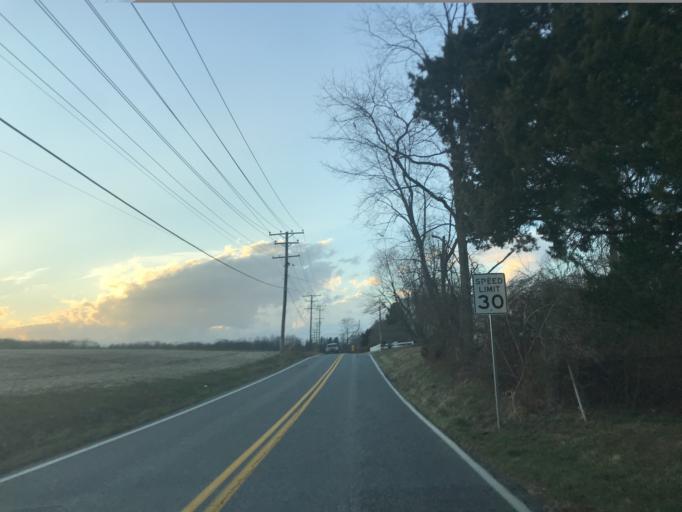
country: US
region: Maryland
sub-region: Harford County
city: Bel Air South
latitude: 39.5199
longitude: -76.2725
